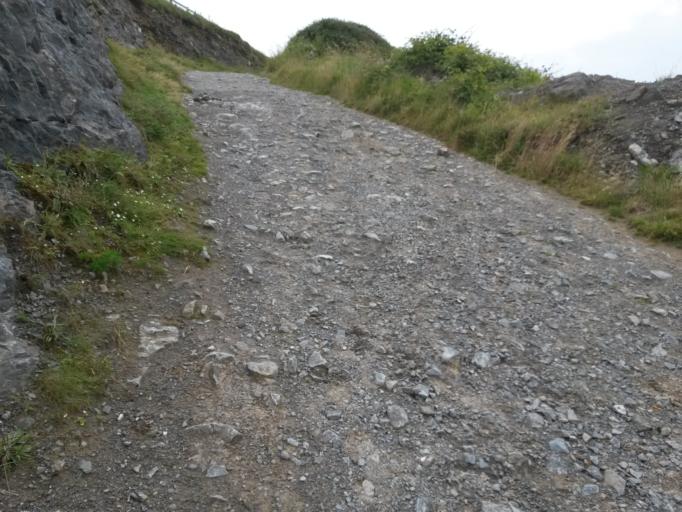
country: IE
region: Ulster
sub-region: County Donegal
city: Bundoran
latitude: 54.4906
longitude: -8.2655
